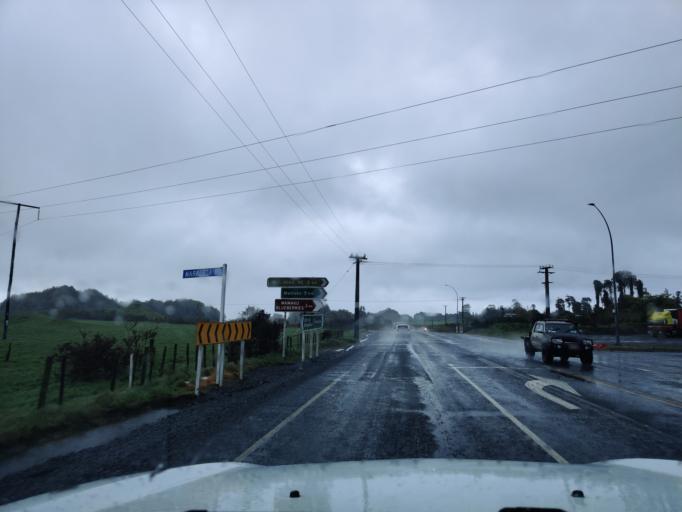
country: NZ
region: Bay of Plenty
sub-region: Rotorua District
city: Rotorua
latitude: -38.0494
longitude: 176.0754
